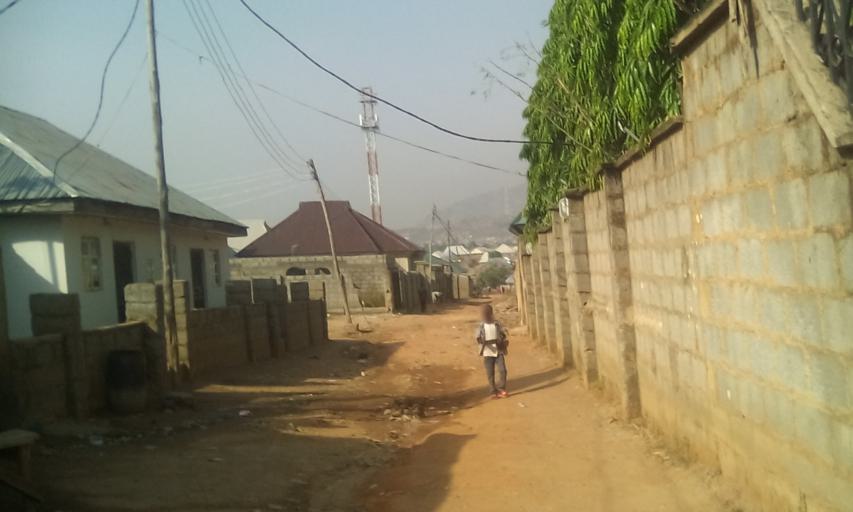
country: NG
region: Abuja Federal Capital Territory
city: Madala
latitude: 9.1085
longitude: 7.2410
